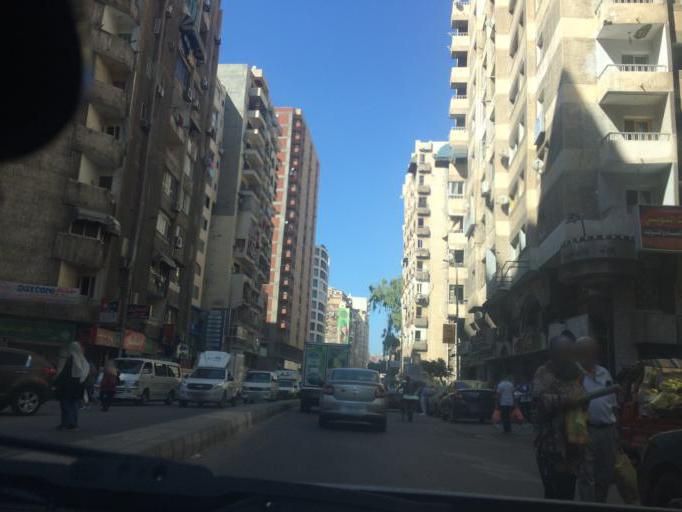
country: EG
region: Alexandria
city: Alexandria
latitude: 31.2715
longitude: 30.0028
